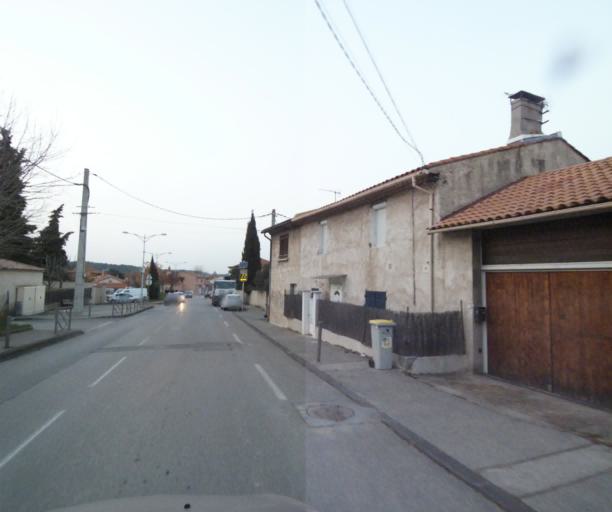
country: FR
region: Provence-Alpes-Cote d'Azur
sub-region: Departement des Bouches-du-Rhone
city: Gardanne
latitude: 43.4322
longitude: 5.4673
